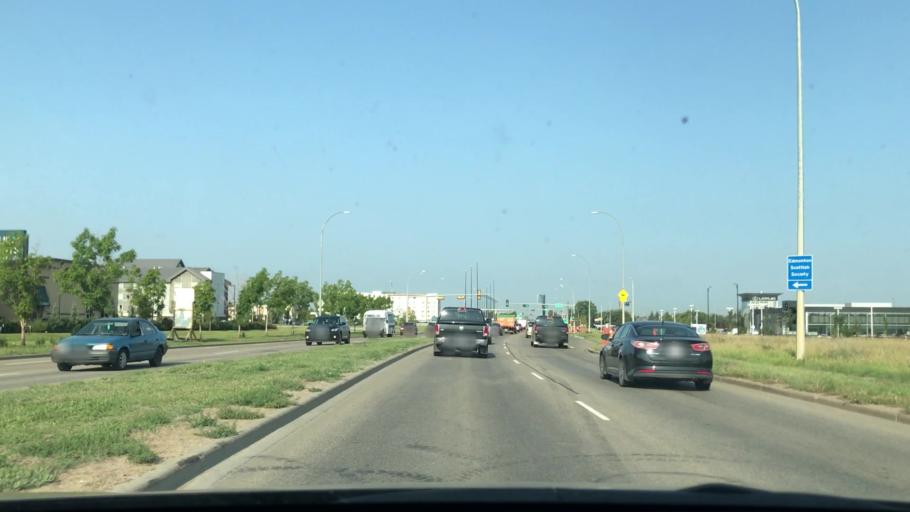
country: CA
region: Alberta
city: Beaumont
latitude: 53.4249
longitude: -113.4866
